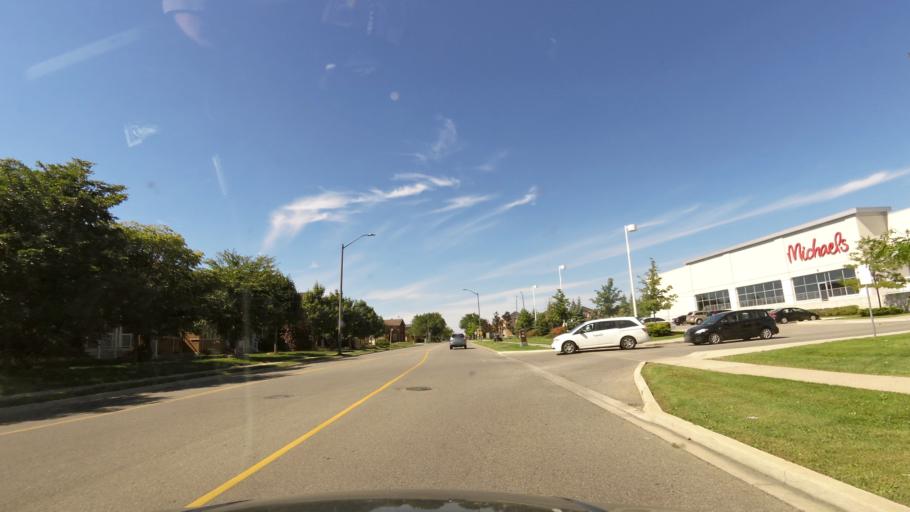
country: CA
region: Ontario
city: Mississauga
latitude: 43.6080
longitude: -79.7019
